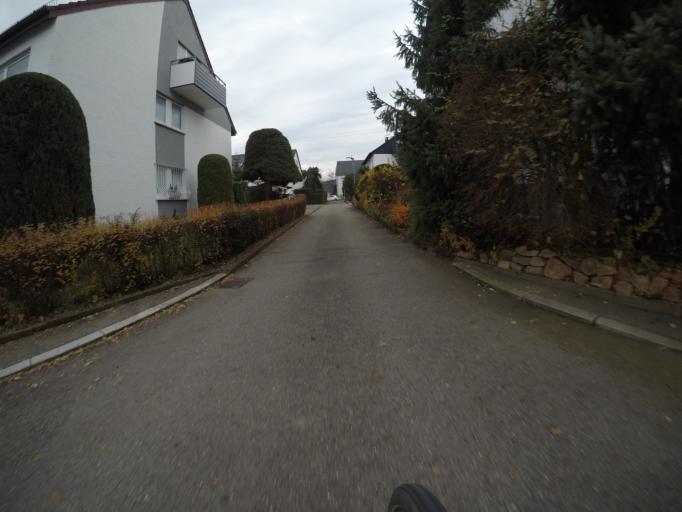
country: DE
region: Baden-Wuerttemberg
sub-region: Regierungsbezirk Stuttgart
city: Leinfelden-Echterdingen
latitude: 48.6901
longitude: 9.1452
